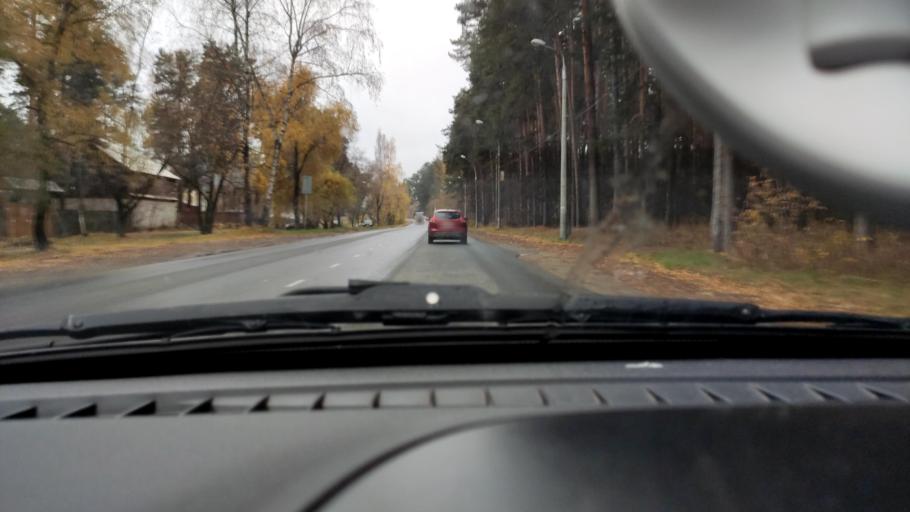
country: RU
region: Perm
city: Kultayevo
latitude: 58.0085
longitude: 55.9748
